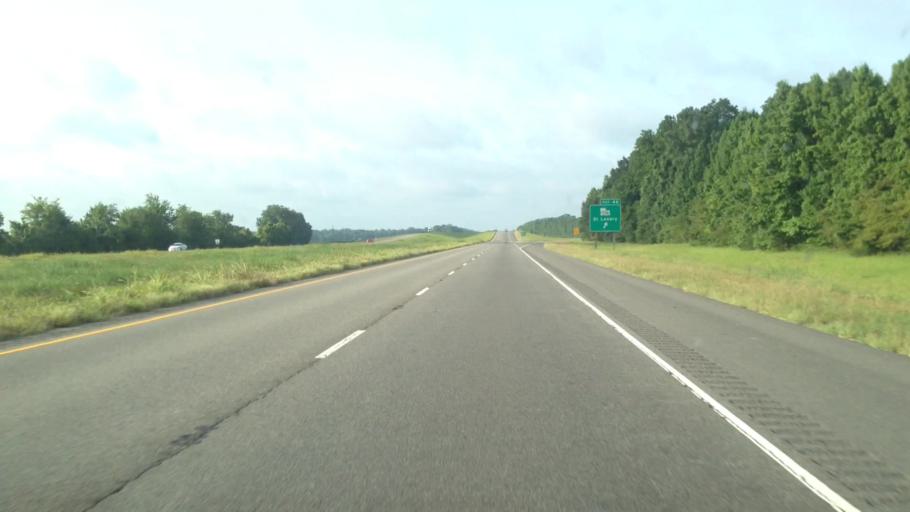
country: US
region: Louisiana
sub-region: Avoyelles Parish
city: Bunkie
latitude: 30.8729
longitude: -92.2280
